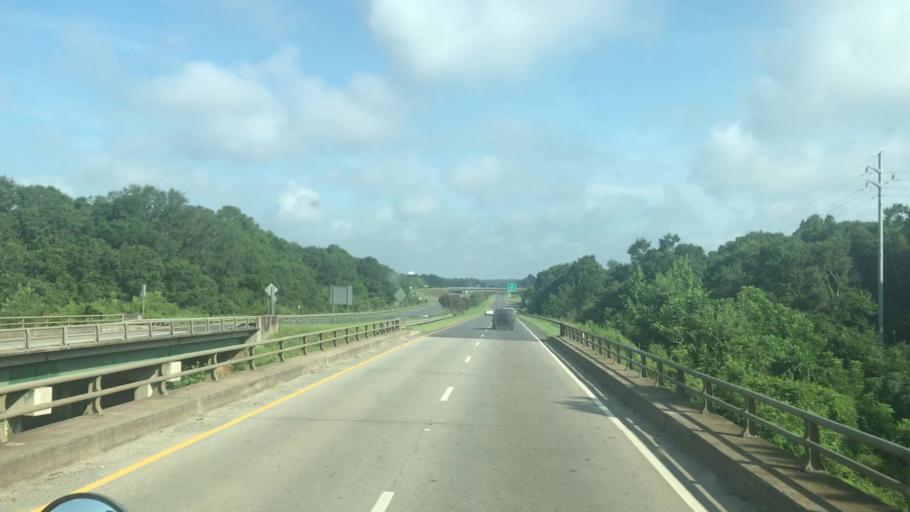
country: US
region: Georgia
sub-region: Decatur County
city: Bainbridge
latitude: 30.9070
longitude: -84.5893
